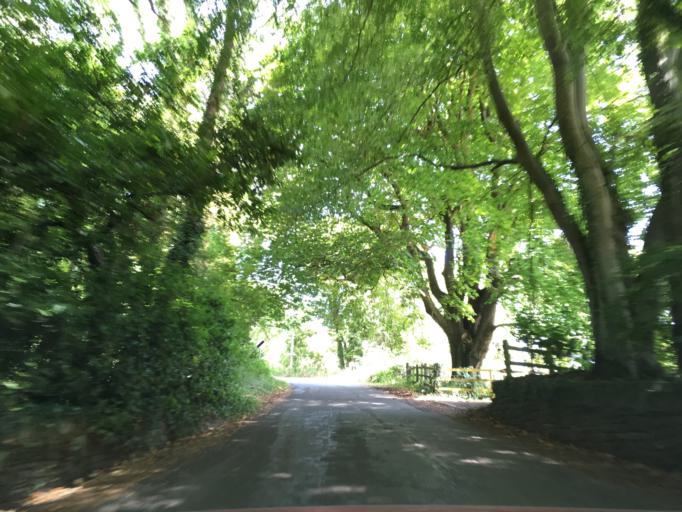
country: GB
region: Wales
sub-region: Caerphilly County Borough
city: Risca
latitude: 51.5863
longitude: -3.1149
